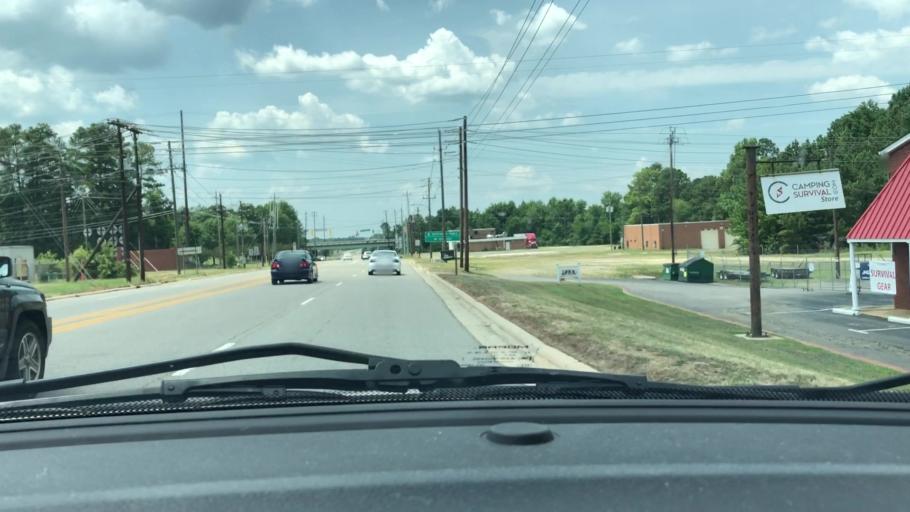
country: US
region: North Carolina
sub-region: Lee County
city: Sanford
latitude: 35.4932
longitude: -79.1924
